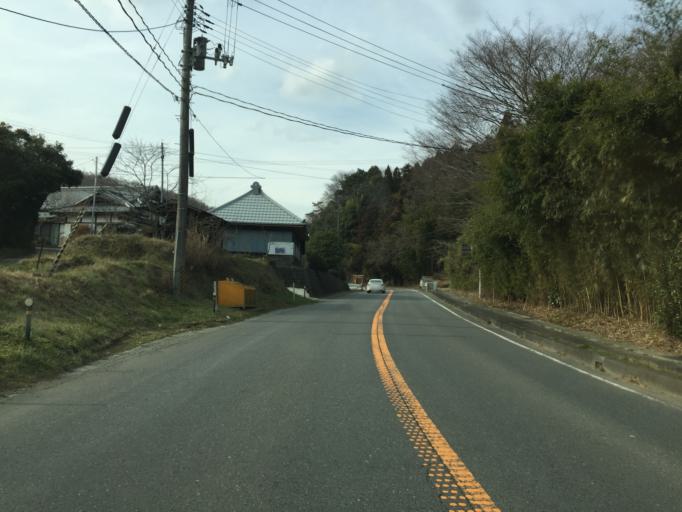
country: JP
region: Fukushima
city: Iwaki
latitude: 36.9662
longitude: 140.7476
